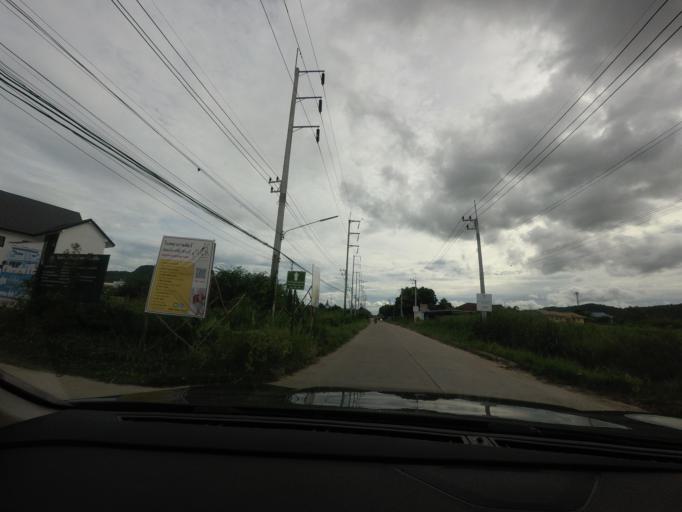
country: TH
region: Prachuap Khiri Khan
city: Hua Hin
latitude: 12.5397
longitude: 99.9483
